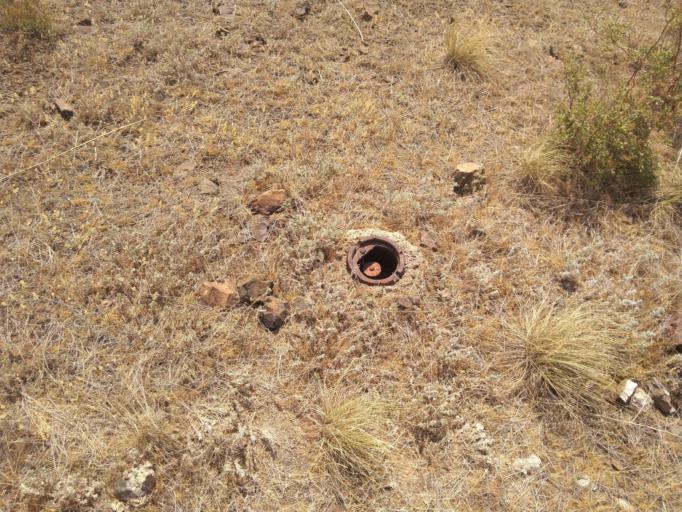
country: RU
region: Orenburg
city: Novotroitsk
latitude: 51.2129
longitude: 58.4119
